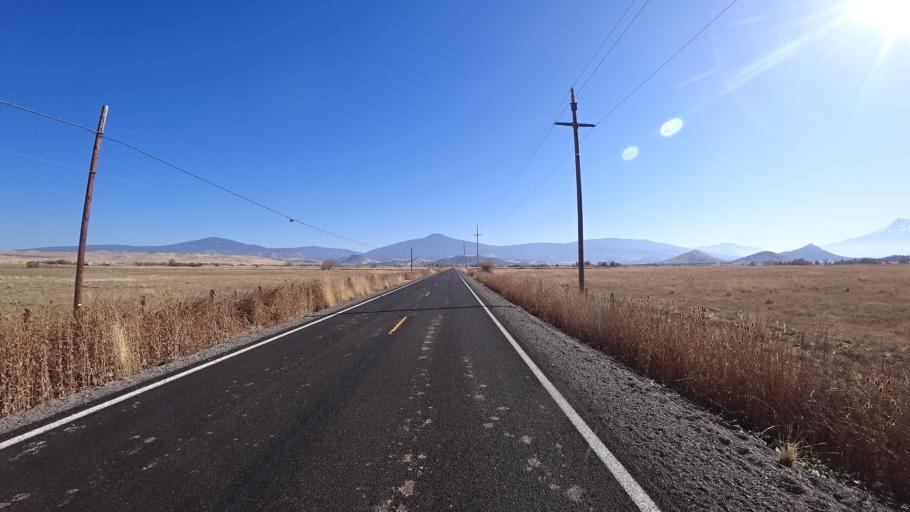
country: US
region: California
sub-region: Siskiyou County
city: Montague
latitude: 41.7114
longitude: -122.4325
